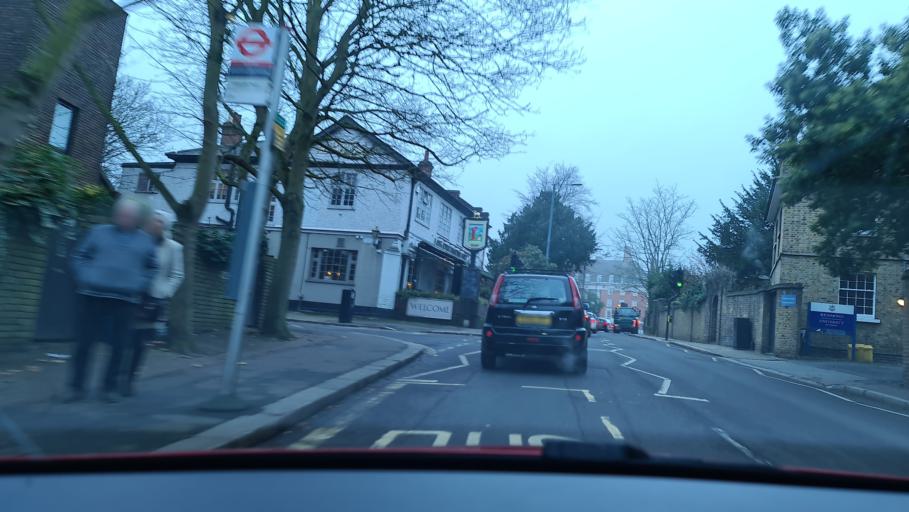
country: GB
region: England
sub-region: Greater London
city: Richmond
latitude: 51.4520
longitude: -0.2954
